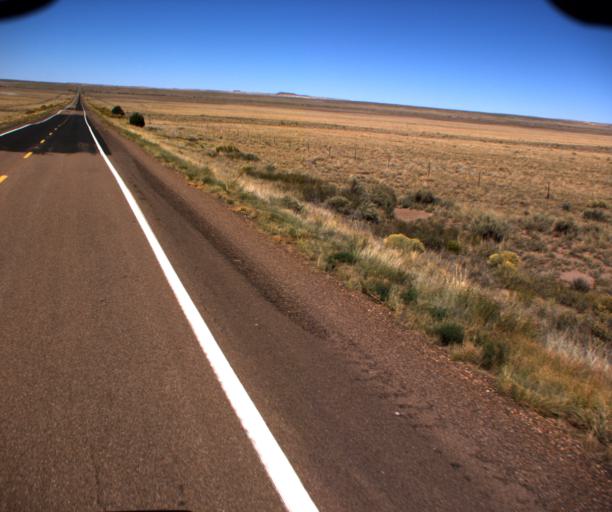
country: US
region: Arizona
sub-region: Navajo County
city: Snowflake
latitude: 34.7204
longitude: -109.7723
